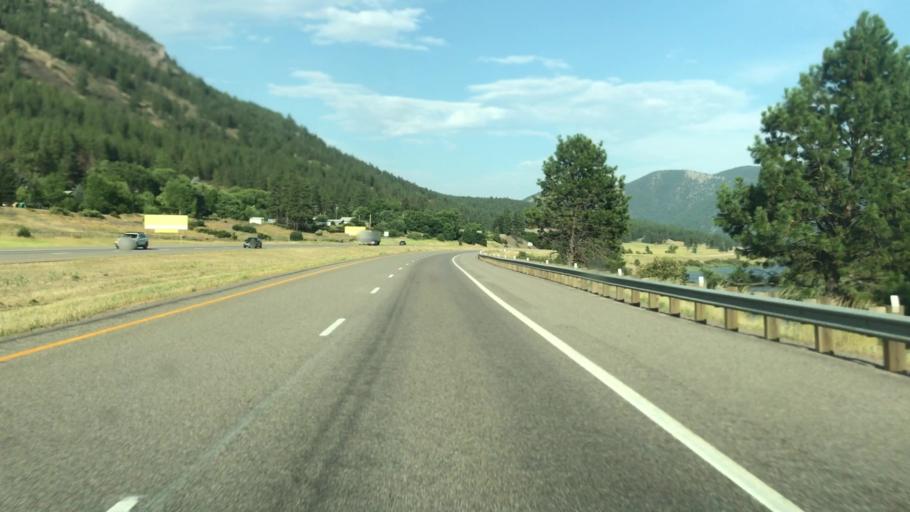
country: US
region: Montana
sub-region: Missoula County
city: Frenchtown
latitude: 47.0007
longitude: -114.4793
